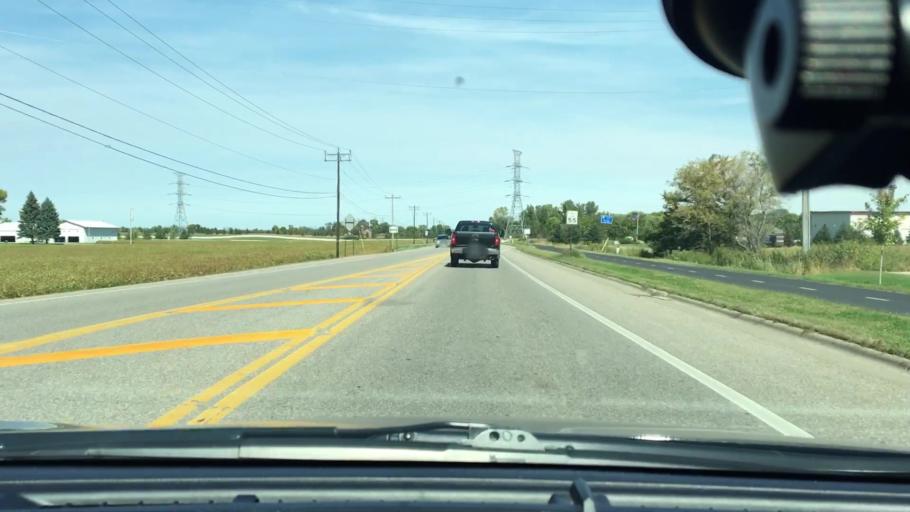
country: US
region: Minnesota
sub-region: Wright County
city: Hanover
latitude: 45.1250
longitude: -93.6357
